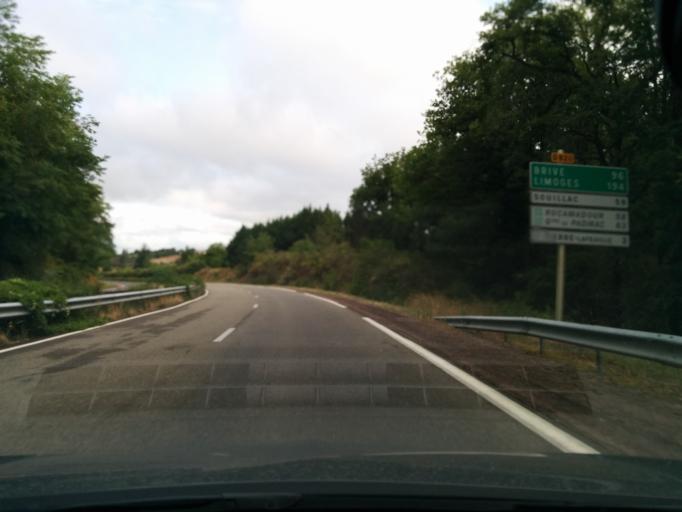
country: FR
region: Midi-Pyrenees
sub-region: Departement du Lot
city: Pradines
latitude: 44.5072
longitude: 1.4459
